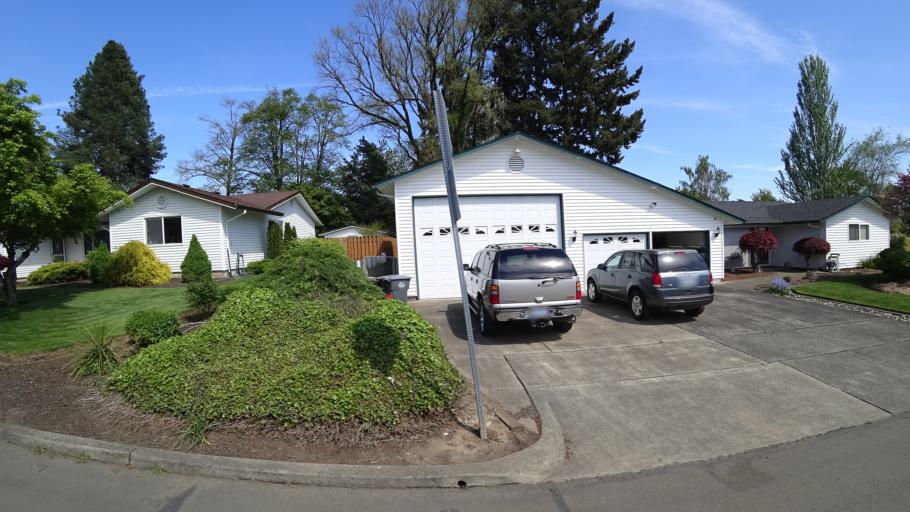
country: US
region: Oregon
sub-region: Washington County
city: Hillsboro
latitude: 45.5112
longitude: -122.9582
